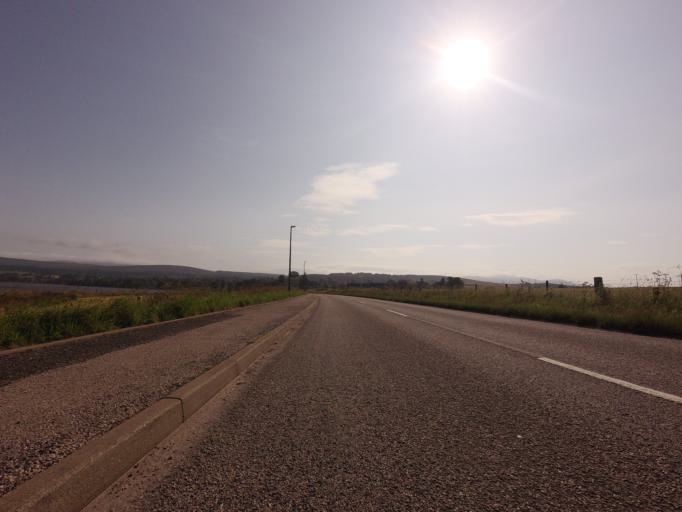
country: GB
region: Scotland
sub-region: Highland
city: Alness
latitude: 57.8863
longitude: -4.3589
